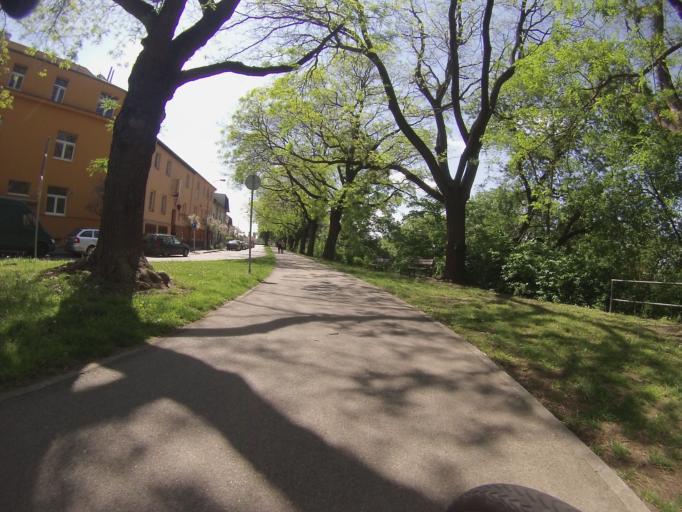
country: CZ
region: South Moravian
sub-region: Mesto Brno
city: Brno
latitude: 49.1768
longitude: 16.6180
